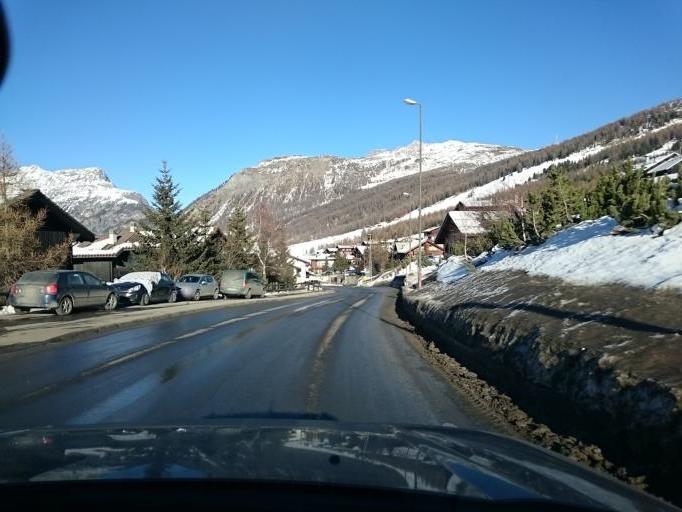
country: IT
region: Lombardy
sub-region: Provincia di Sondrio
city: Livigno
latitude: 46.5314
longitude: 10.1383
